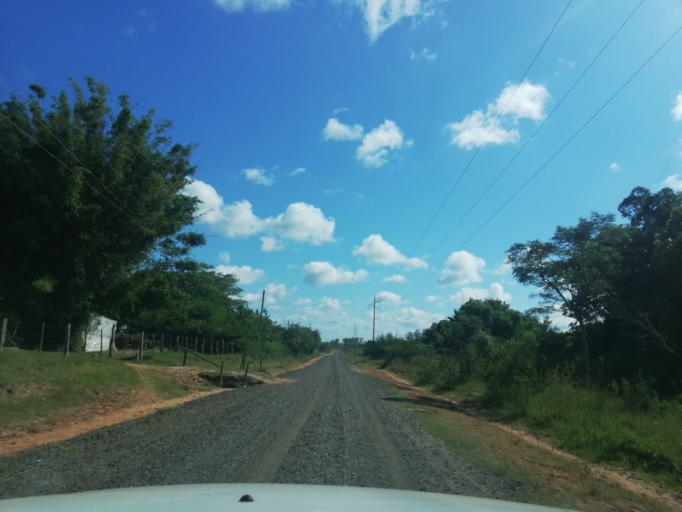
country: AR
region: Corrientes
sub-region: Departamento de San Miguel
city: San Miguel
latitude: -27.9863
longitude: -57.5845
